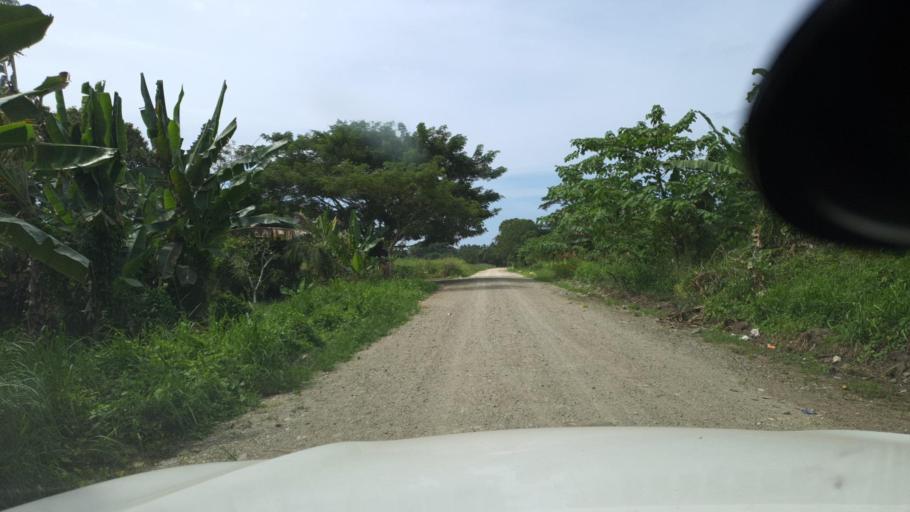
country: SB
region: Guadalcanal
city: Honiara
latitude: -9.4152
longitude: 159.8898
